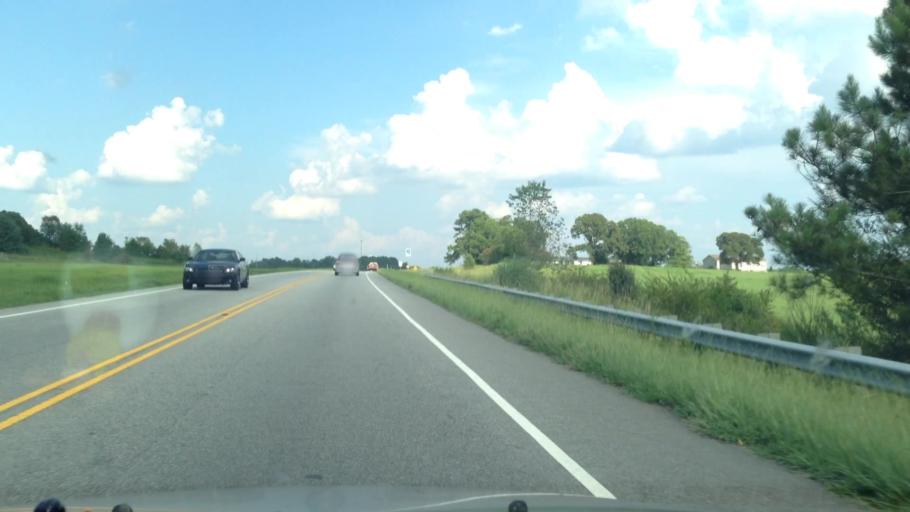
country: US
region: North Carolina
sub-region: Lee County
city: Broadway
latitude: 35.4390
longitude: -79.0434
